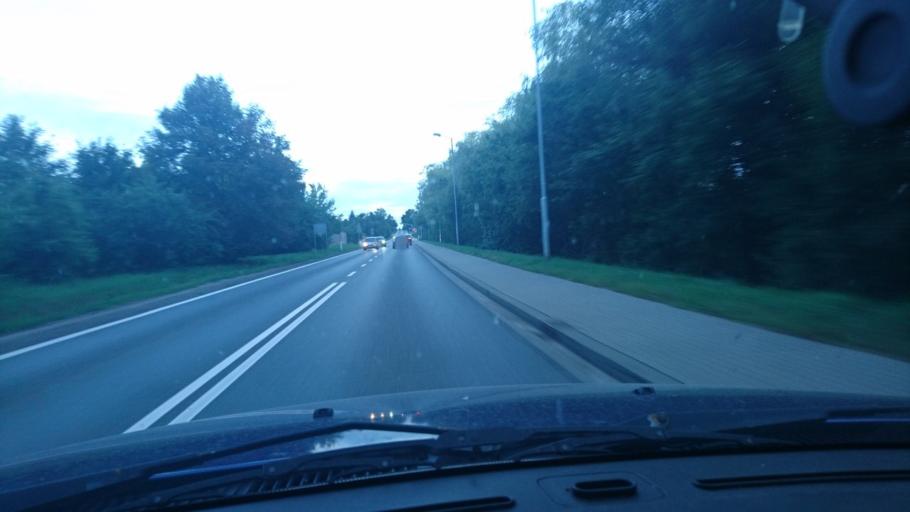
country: PL
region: Silesian Voivodeship
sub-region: Powiat tarnogorski
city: Tarnowskie Gory
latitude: 50.4489
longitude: 18.8372
